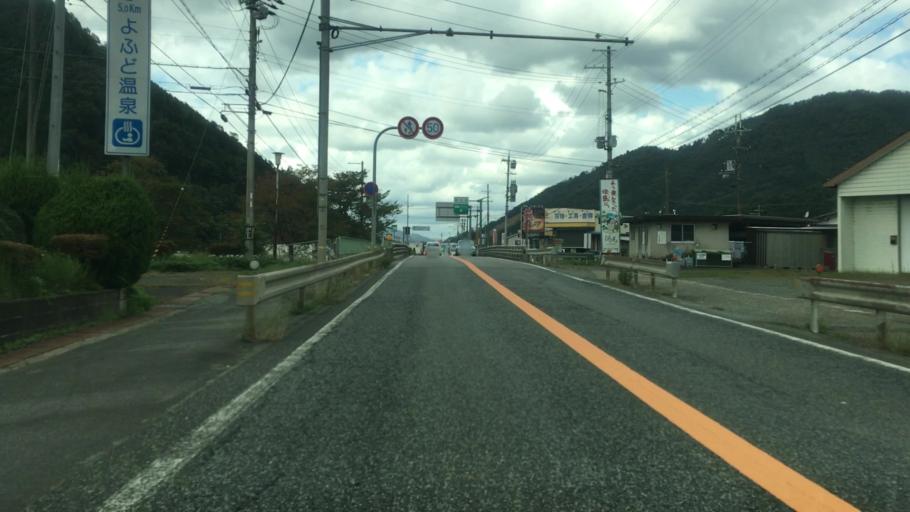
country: JP
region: Hyogo
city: Toyooka
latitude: 35.3200
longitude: 134.8810
